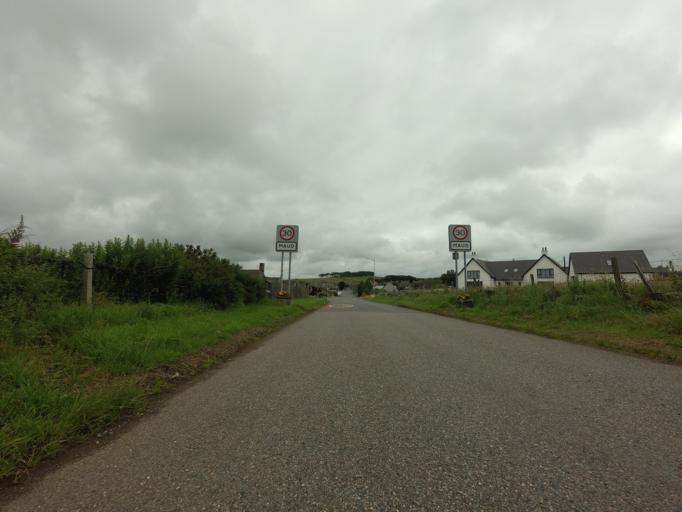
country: GB
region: Scotland
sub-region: Aberdeenshire
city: Mintlaw
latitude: 57.5232
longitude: -2.1338
